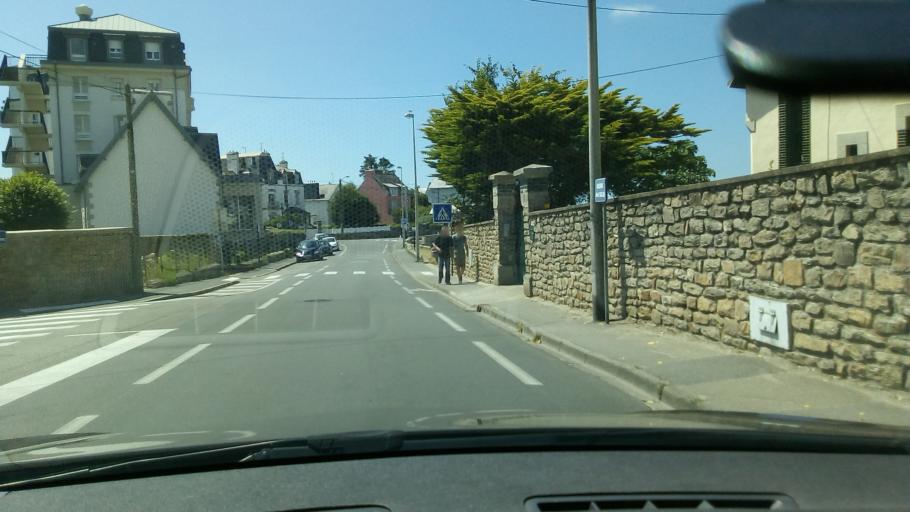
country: FR
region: Brittany
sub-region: Departement du Finistere
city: Concarneau
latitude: 47.8747
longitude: -3.9287
